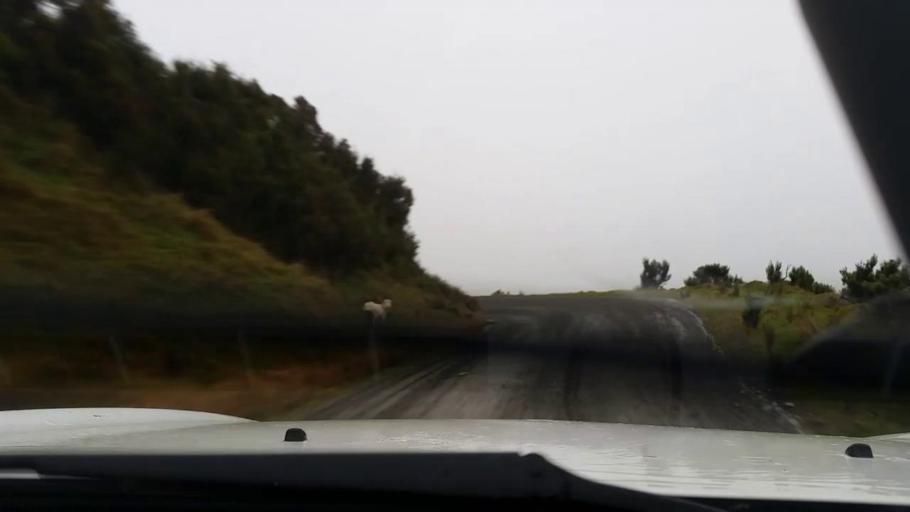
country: NZ
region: Wellington
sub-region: Masterton District
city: Masterton
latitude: -41.2478
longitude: 175.8799
